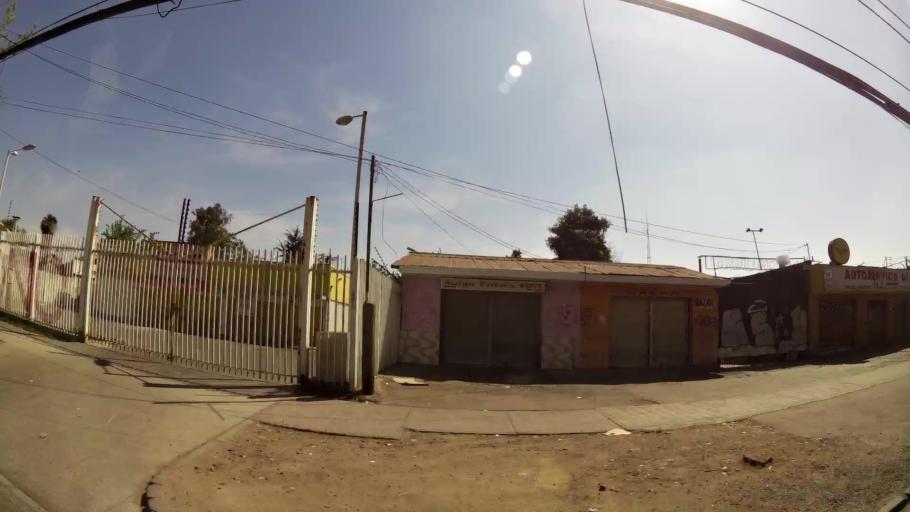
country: CL
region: Santiago Metropolitan
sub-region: Provincia de Santiago
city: Villa Presidente Frei, Nunoa, Santiago, Chile
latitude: -33.4848
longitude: -70.5851
